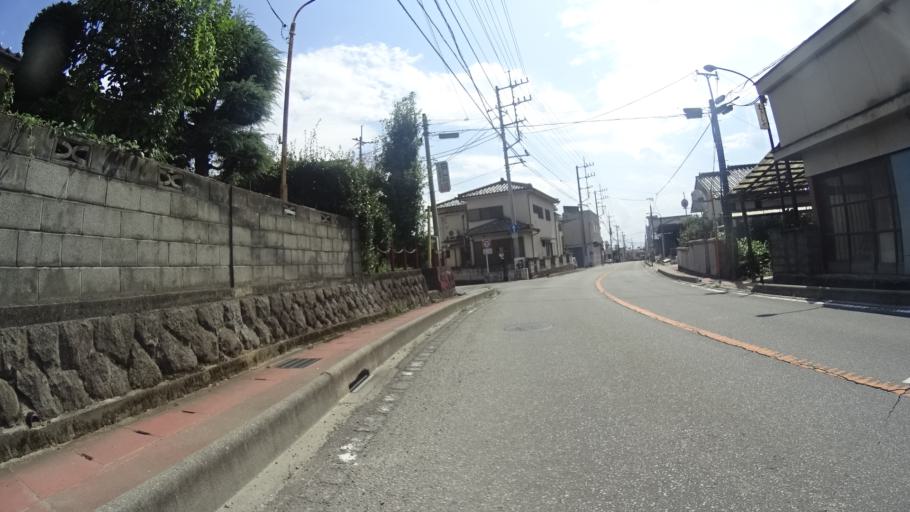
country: JP
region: Yamanashi
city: Enzan
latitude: 35.7111
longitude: 138.7329
